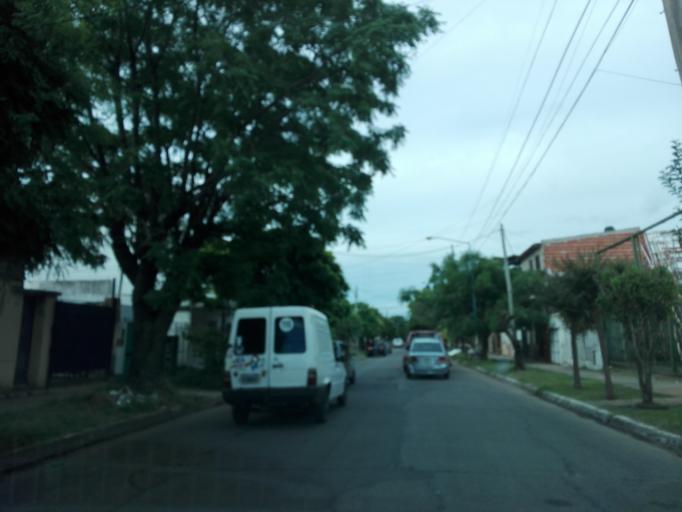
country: AR
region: Buenos Aires
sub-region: Partido de Lanus
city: Lanus
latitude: -34.7202
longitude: -58.3829
